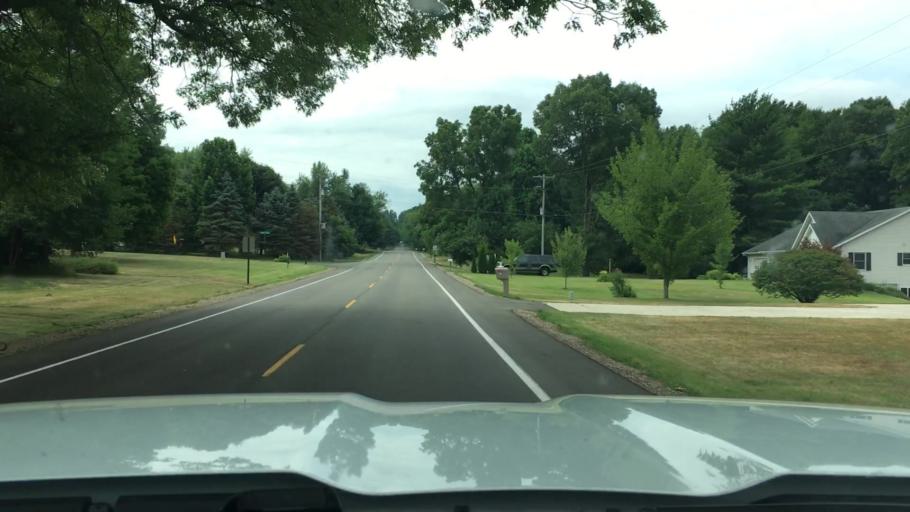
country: US
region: Michigan
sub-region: Allegan County
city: Plainwell
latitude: 42.4584
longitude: -85.6027
